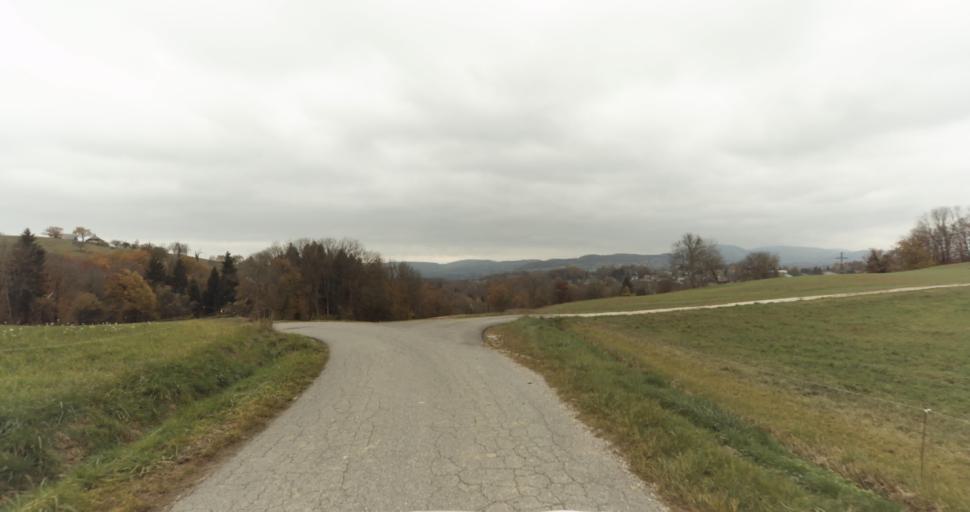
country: FR
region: Rhone-Alpes
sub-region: Departement de la Haute-Savoie
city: Chavanod
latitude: 45.8703
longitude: 6.0405
